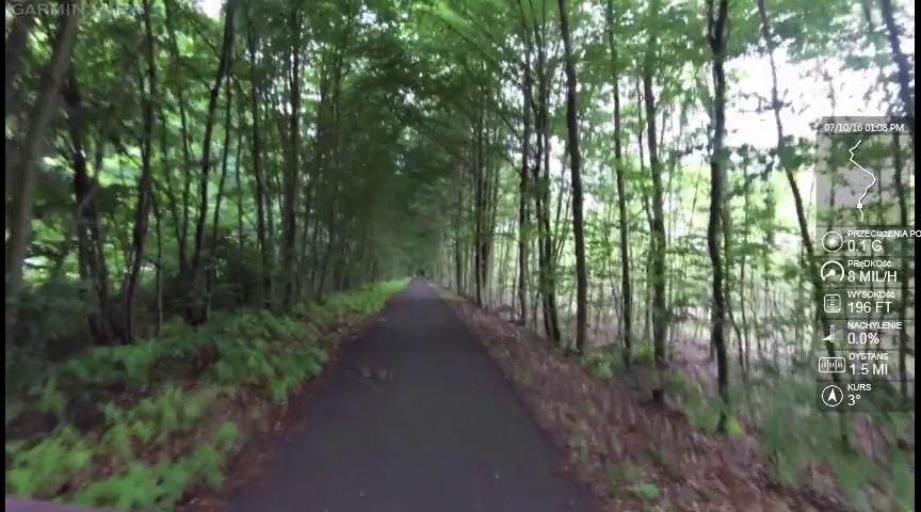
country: PL
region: West Pomeranian Voivodeship
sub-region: Powiat gryfinski
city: Banie
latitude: 53.0585
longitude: 14.6274
